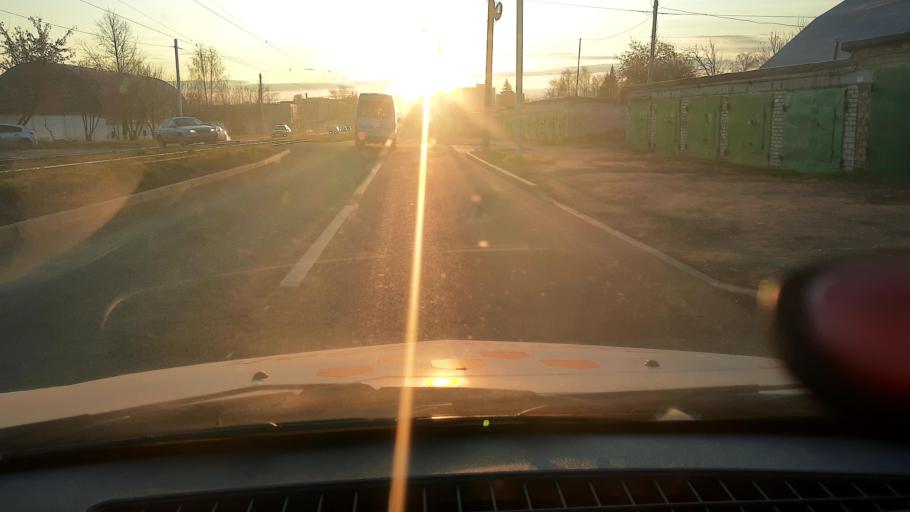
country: RU
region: Bashkortostan
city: Ufa
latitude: 54.8248
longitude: 56.0957
